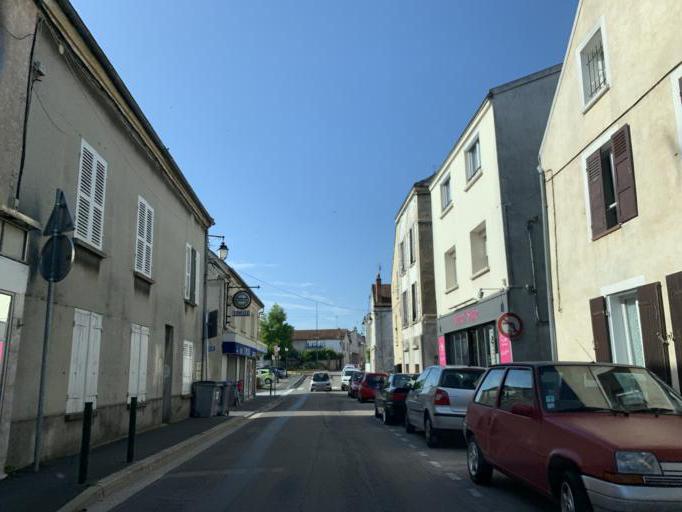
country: FR
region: Ile-de-France
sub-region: Departement de Seine-et-Marne
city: Annet-sur-Marne
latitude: 48.9275
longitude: 2.7200
